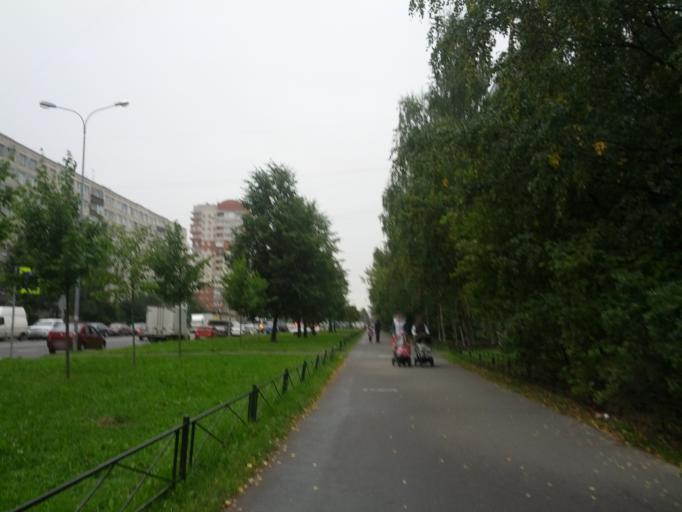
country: RU
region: St.-Petersburg
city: Obukhovo
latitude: 59.9016
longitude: 30.4712
